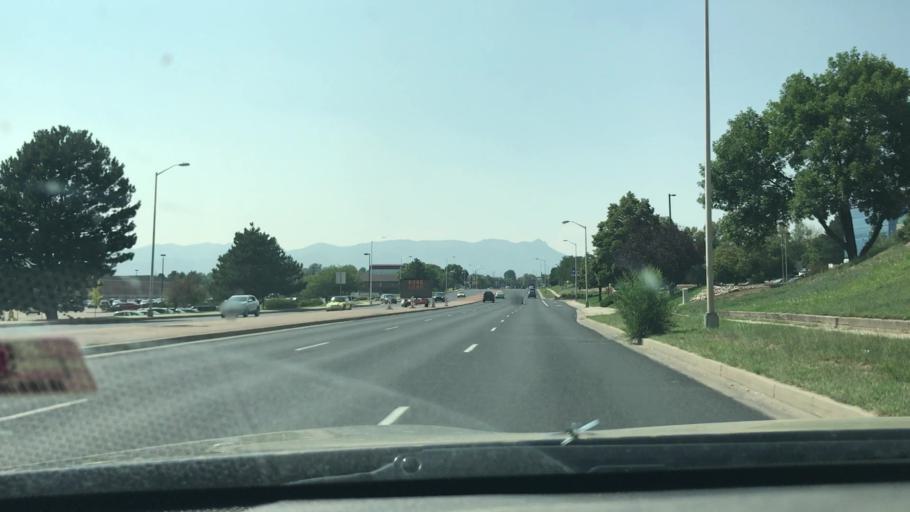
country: US
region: Colorado
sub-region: El Paso County
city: Colorado Springs
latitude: 38.9052
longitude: -104.7770
